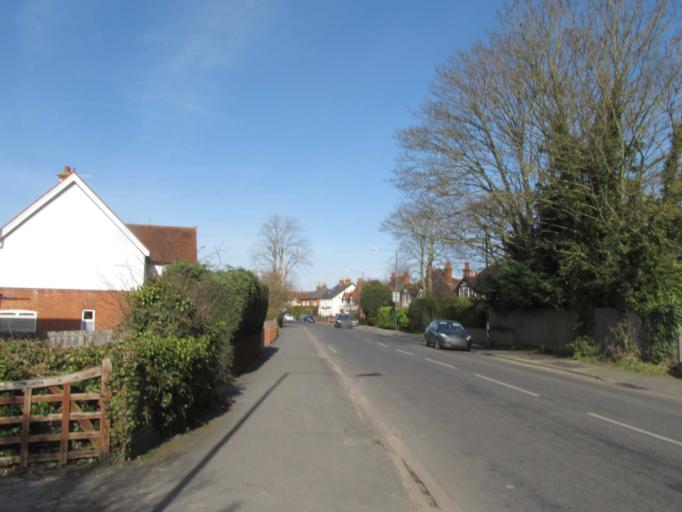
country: GB
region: England
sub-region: Royal Borough of Windsor and Maidenhead
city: Maidenhead
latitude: 51.5316
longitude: -0.7388
